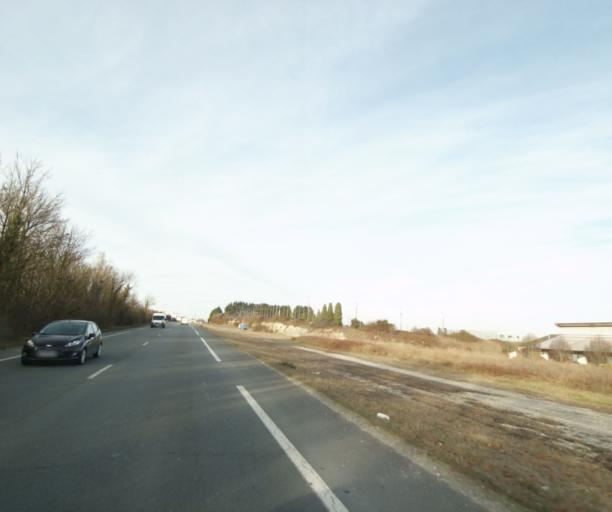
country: FR
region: Poitou-Charentes
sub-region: Departement de la Charente-Maritime
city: Saintes
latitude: 45.7411
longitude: -0.6608
